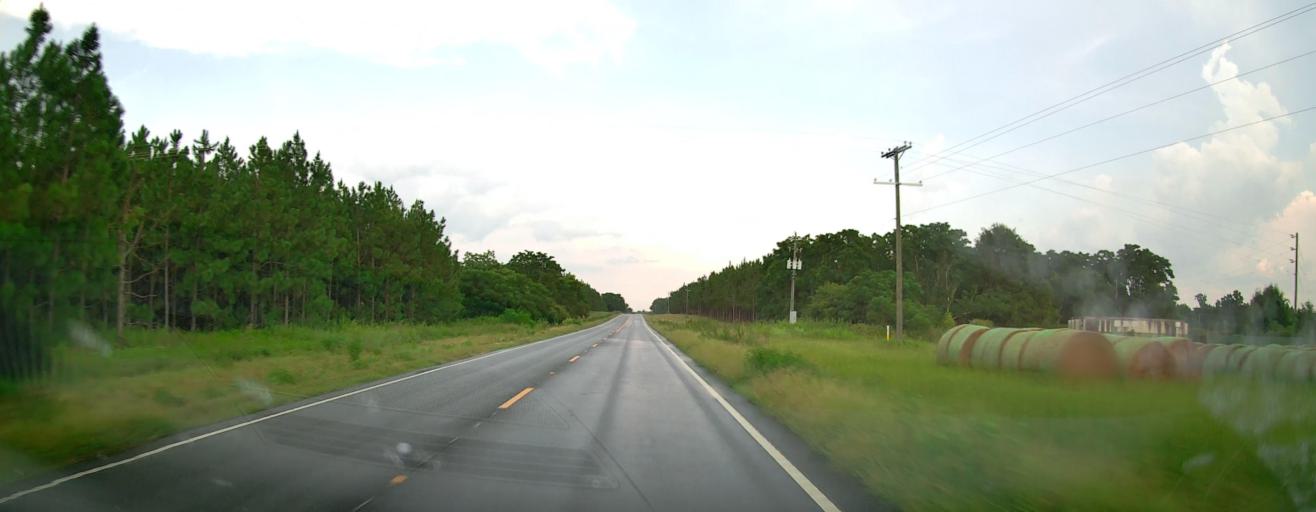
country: US
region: Georgia
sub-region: Dodge County
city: Chester
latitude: 32.5506
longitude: -83.1321
